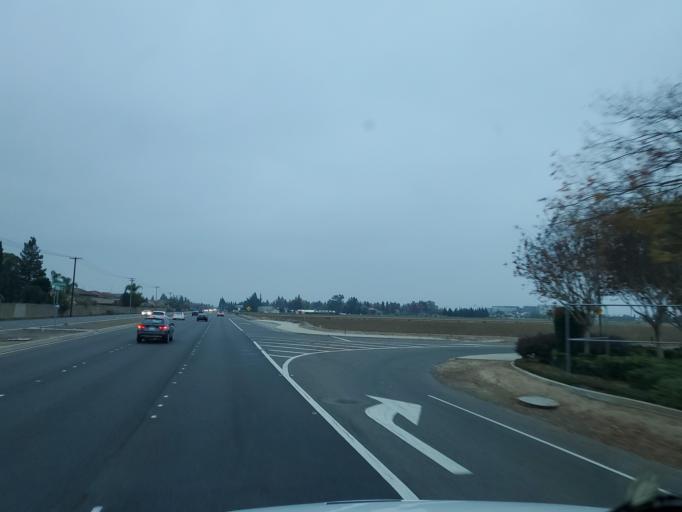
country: US
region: California
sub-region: Stanislaus County
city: Salida
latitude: 37.7005
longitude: -121.0404
